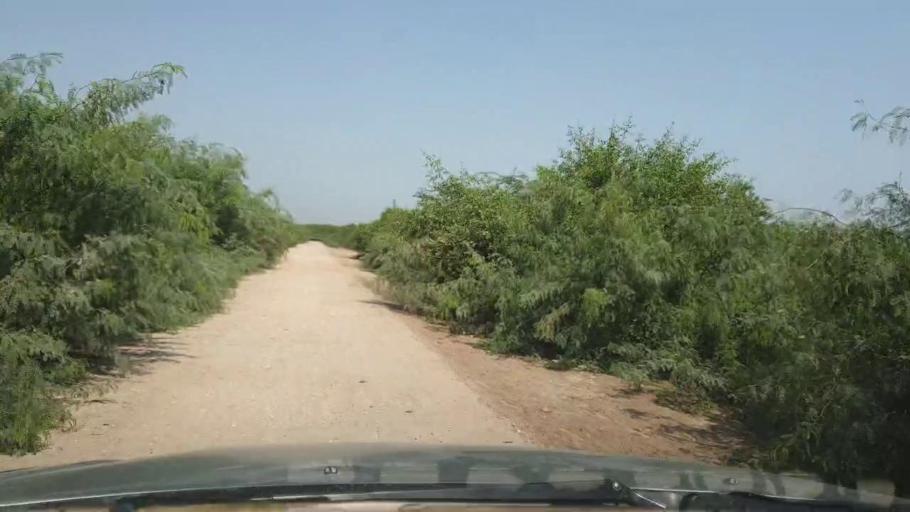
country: PK
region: Sindh
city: Chambar
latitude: 25.2324
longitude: 68.7735
